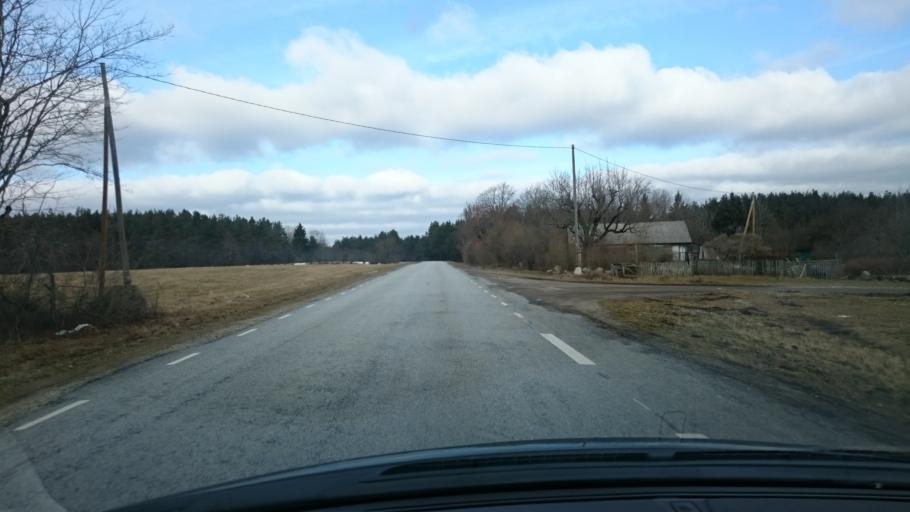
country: EE
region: Harju
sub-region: Keila linn
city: Keila
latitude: 59.3604
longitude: 24.3385
